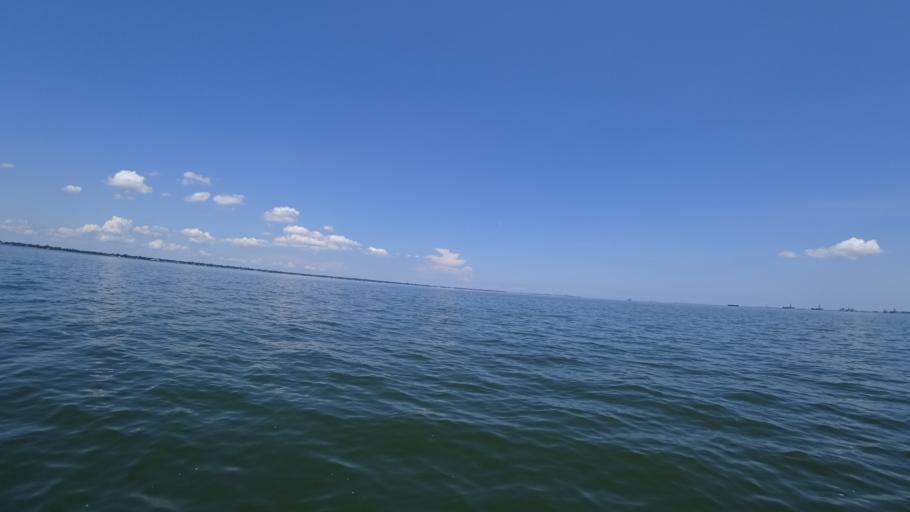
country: US
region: Virginia
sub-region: City of Newport News
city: Newport News
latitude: 36.9536
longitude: -76.3858
